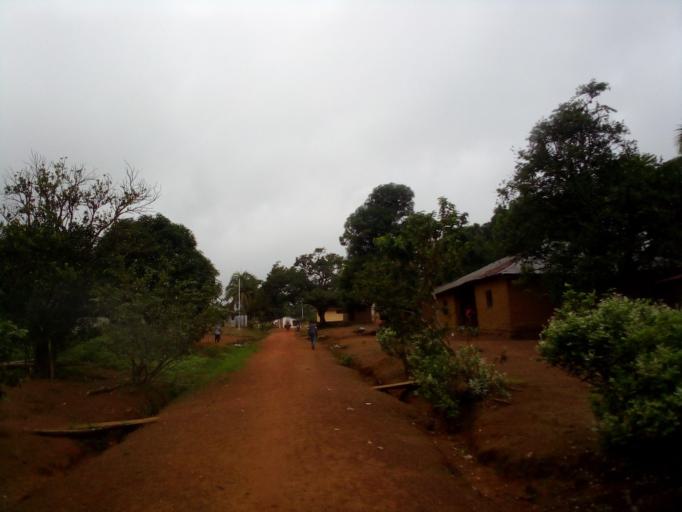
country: SL
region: Eastern Province
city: Kailahun
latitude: 8.2493
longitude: -10.6074
